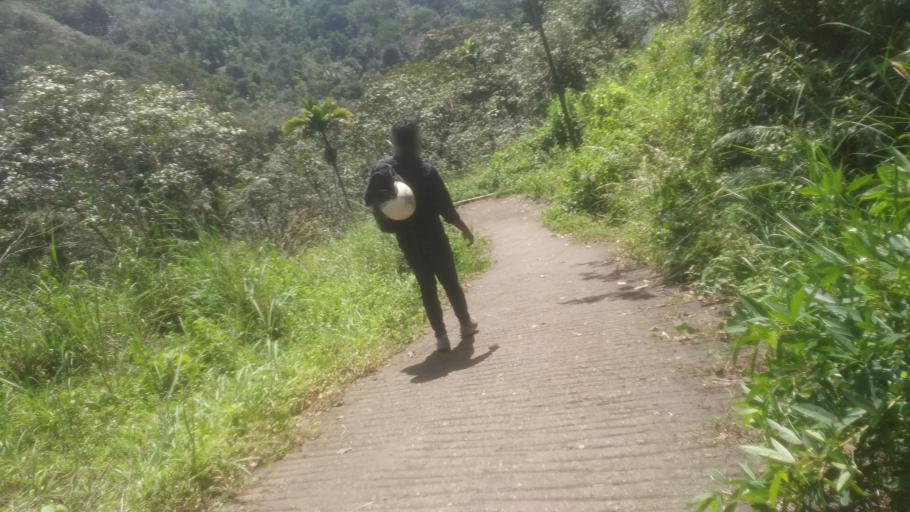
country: IN
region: Kerala
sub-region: Idukki
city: Idukki
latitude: 9.9746
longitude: 76.8381
